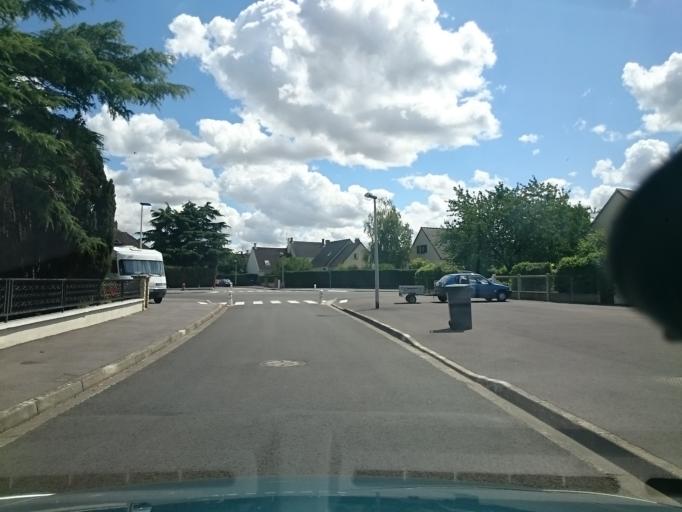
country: FR
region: Lower Normandy
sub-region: Departement du Calvados
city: Ifs
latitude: 49.1438
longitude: -0.3545
